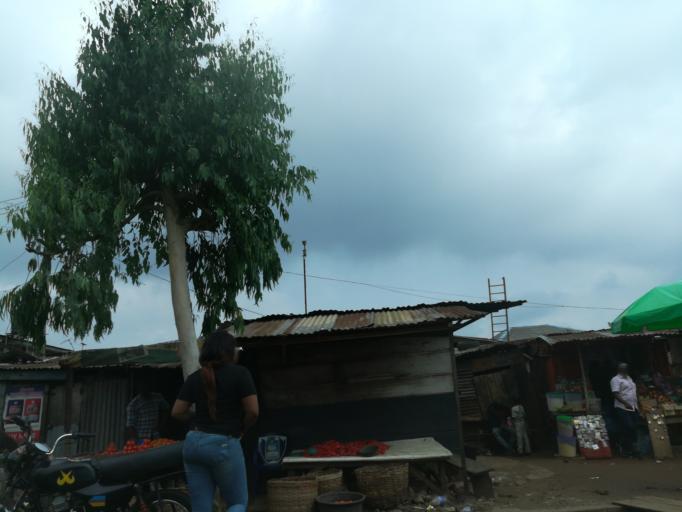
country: NG
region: Lagos
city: Agege
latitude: 6.5840
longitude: 3.3061
